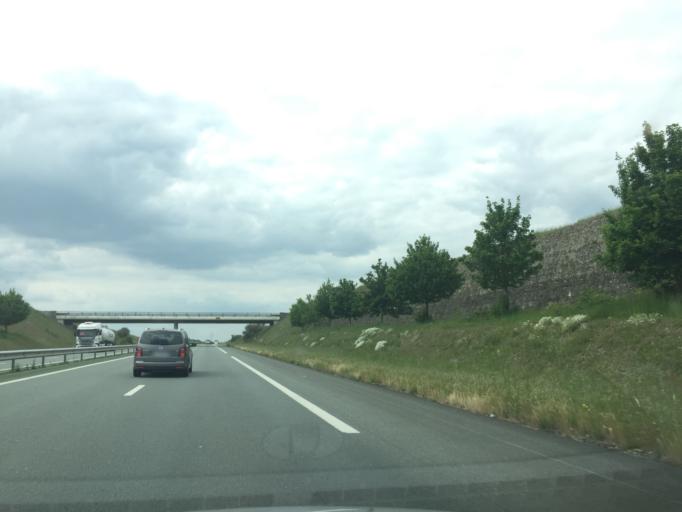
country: FR
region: Poitou-Charentes
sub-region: Departement des Deux-Sevres
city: Saint-Maxire
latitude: 46.4244
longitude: -0.4615
